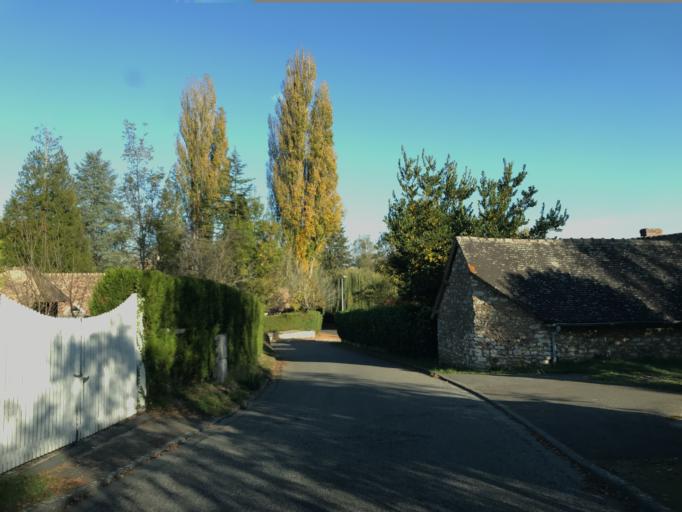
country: FR
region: Haute-Normandie
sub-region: Departement de l'Eure
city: Houlbec-Cocherel
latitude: 49.0726
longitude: 1.2827
